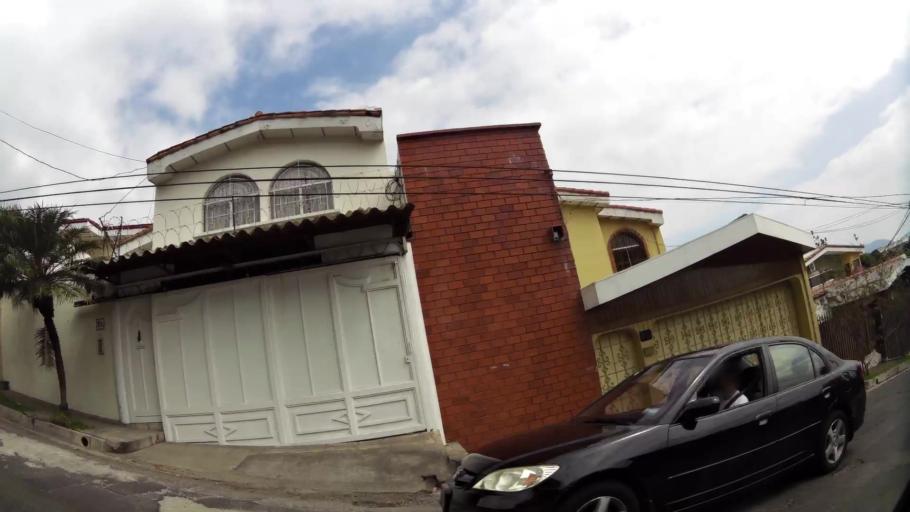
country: SV
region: La Libertad
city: Santa Tecla
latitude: 13.7071
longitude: -89.2616
